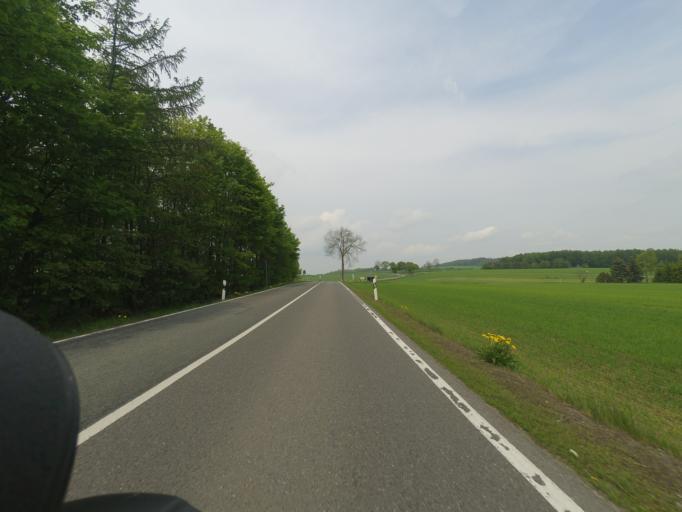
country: DE
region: Saxony
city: Zoblitz
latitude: 50.6485
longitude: 13.2826
